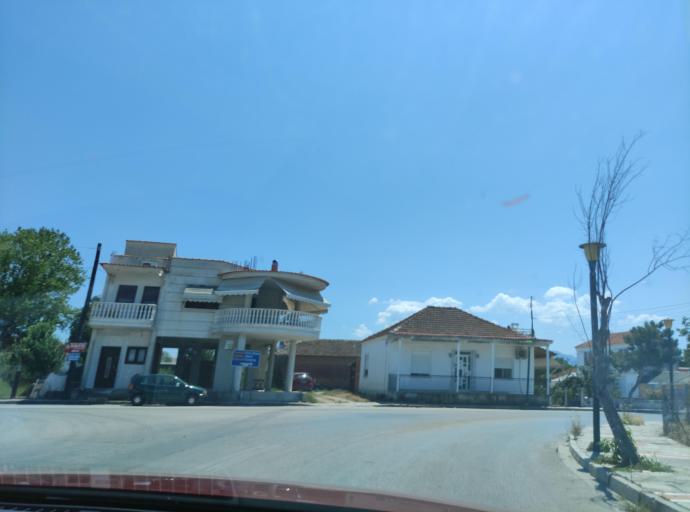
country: GR
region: East Macedonia and Thrace
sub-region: Nomos Kavalas
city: Keramoti
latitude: 40.8596
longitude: 24.7058
